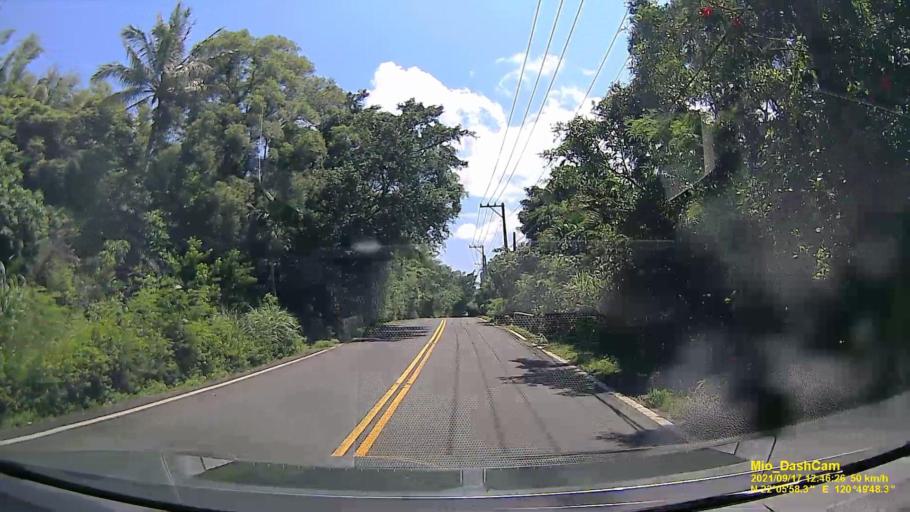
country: TW
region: Taiwan
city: Hengchun
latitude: 22.0994
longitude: 120.8301
